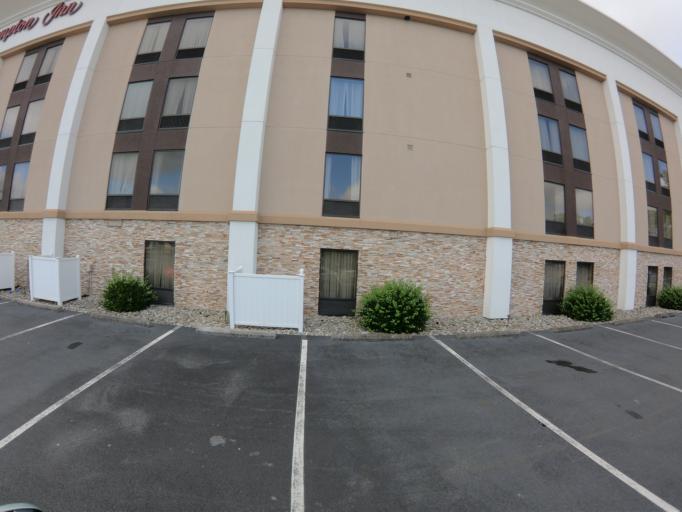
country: US
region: Delaware
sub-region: Sussex County
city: Lewes
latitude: 38.7324
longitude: -75.1359
